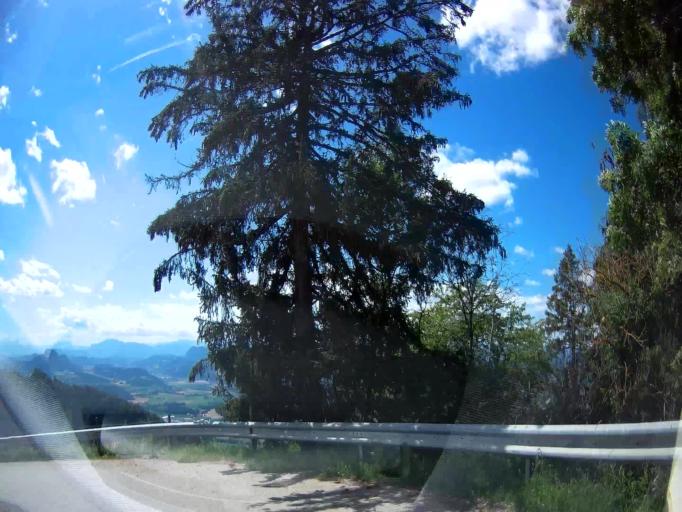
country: AT
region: Carinthia
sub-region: Politischer Bezirk Sankt Veit an der Glan
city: St. Georgen am Laengsee
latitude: 46.7288
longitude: 14.4279
